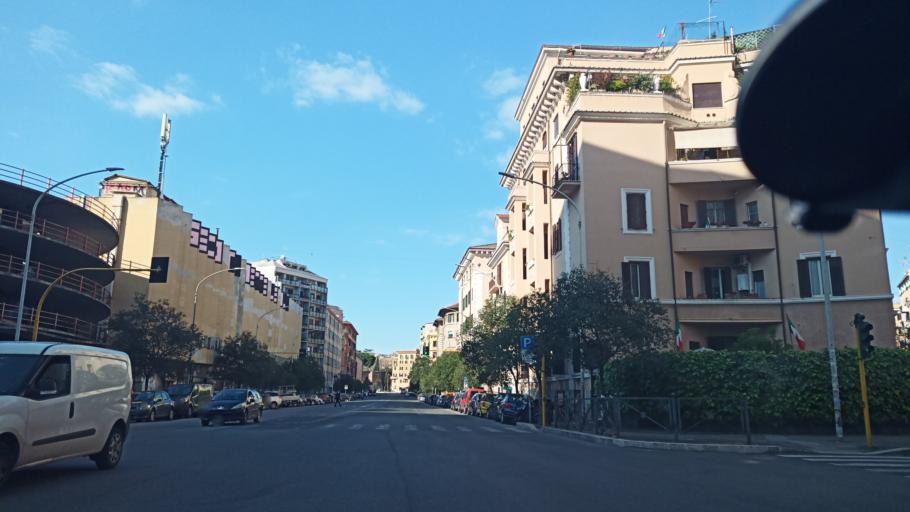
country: IT
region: Latium
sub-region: Citta metropolitana di Roma Capitale
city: Rome
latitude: 41.8821
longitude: 12.5083
